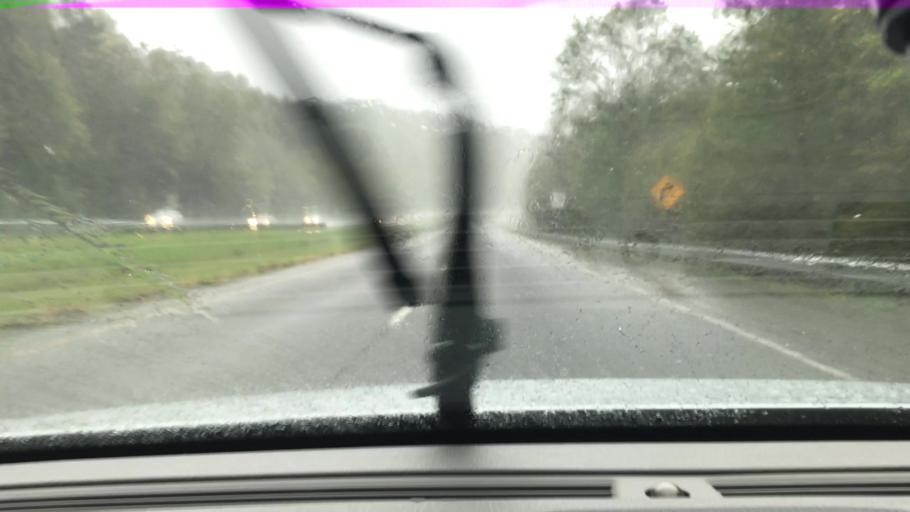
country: US
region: Alabama
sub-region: Limestone County
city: Ardmore
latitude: 34.9821
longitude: -86.8794
